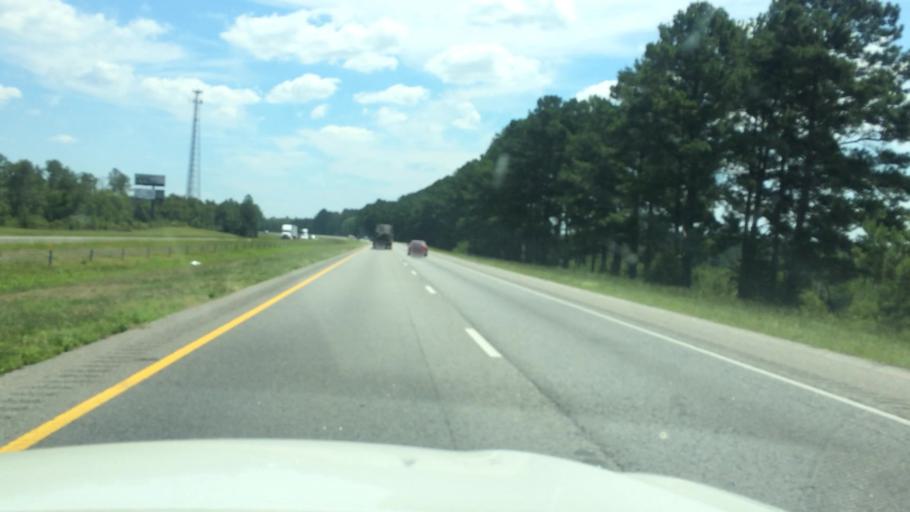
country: US
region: South Carolina
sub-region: Aiken County
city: Aiken
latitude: 33.6807
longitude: -81.6297
